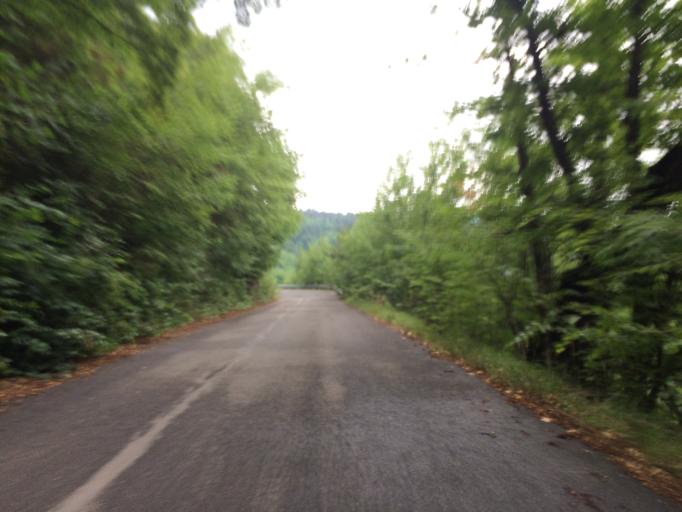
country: IT
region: Liguria
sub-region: Provincia di Imperia
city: Triora
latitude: 43.9792
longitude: 7.7465
